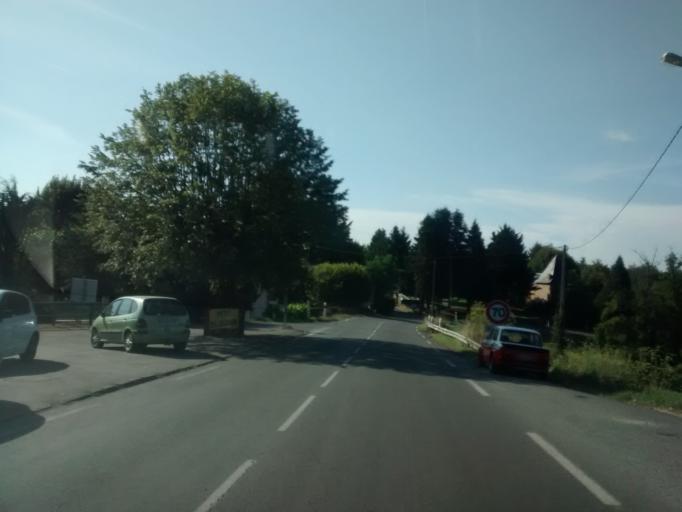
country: FR
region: Aquitaine
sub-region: Departement de la Dordogne
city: Sarlat-la-Caneda
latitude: 44.9226
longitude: 1.2064
